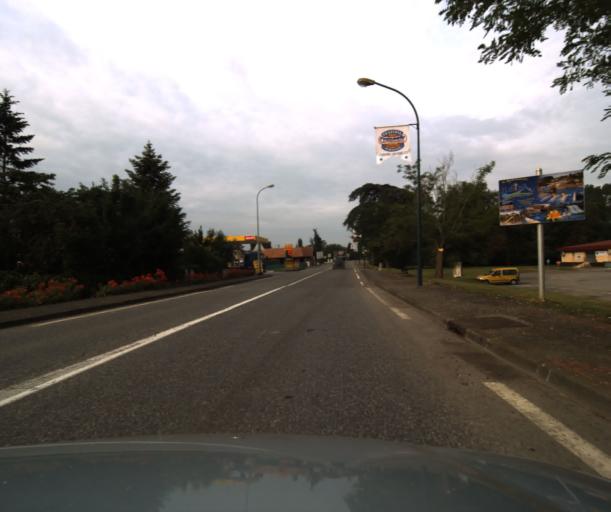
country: FR
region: Midi-Pyrenees
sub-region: Departement du Gers
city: Mirande
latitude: 43.5172
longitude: 0.4137
